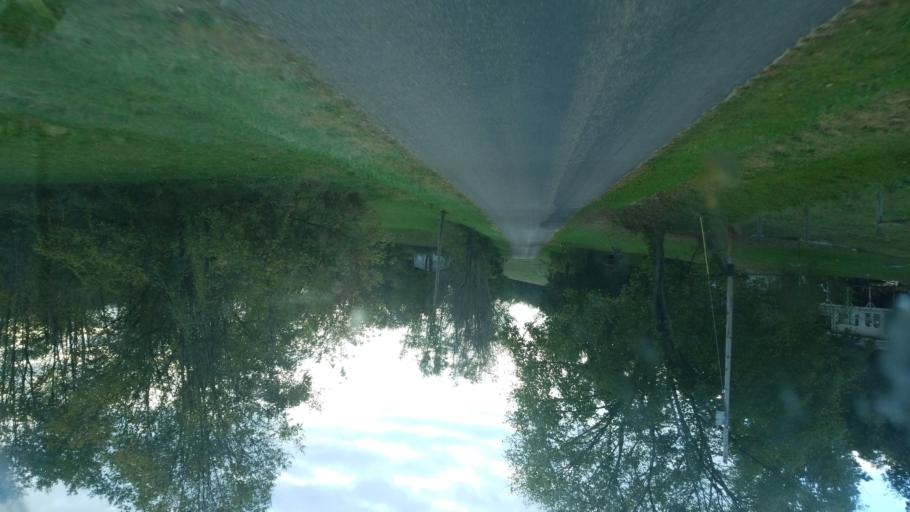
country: US
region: Ohio
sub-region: Ashland County
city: Loudonville
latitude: 40.6998
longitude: -82.2352
